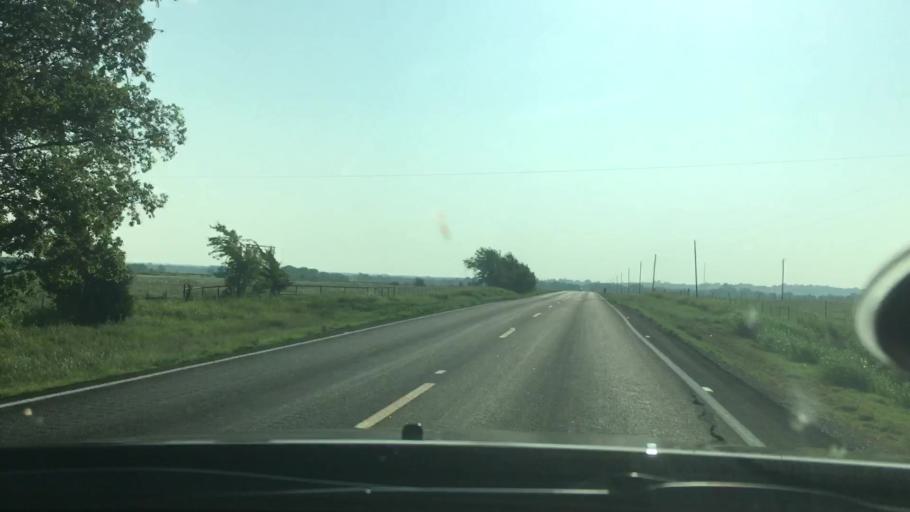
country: US
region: Oklahoma
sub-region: Bryan County
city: Durant
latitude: 34.1426
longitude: -96.3016
